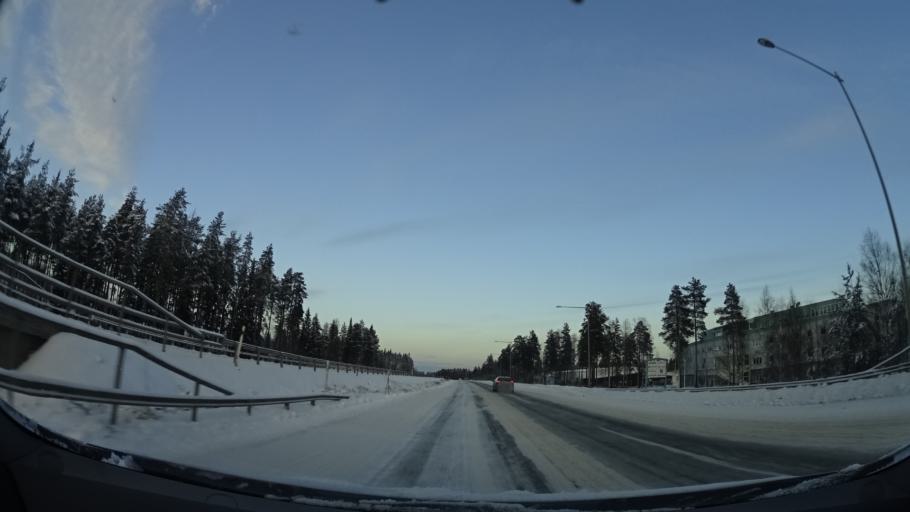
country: SE
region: Vaesterbotten
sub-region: Skelleftea Kommun
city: Skelleftea
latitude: 64.7680
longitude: 21.0175
